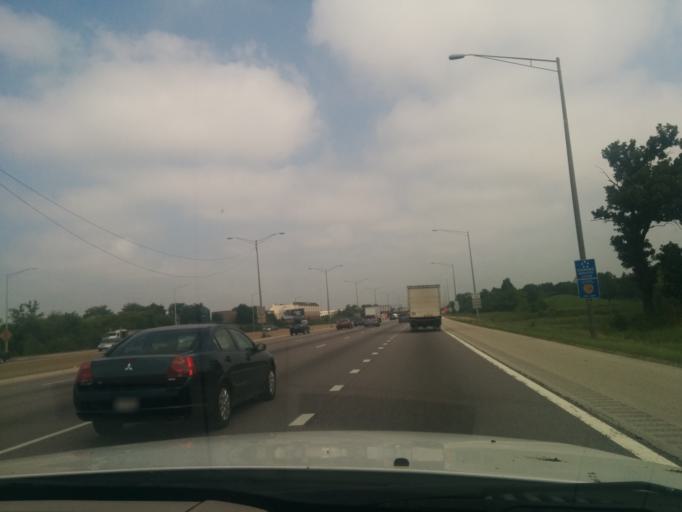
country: US
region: Illinois
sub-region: DuPage County
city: Itasca
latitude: 41.9660
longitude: -88.0255
